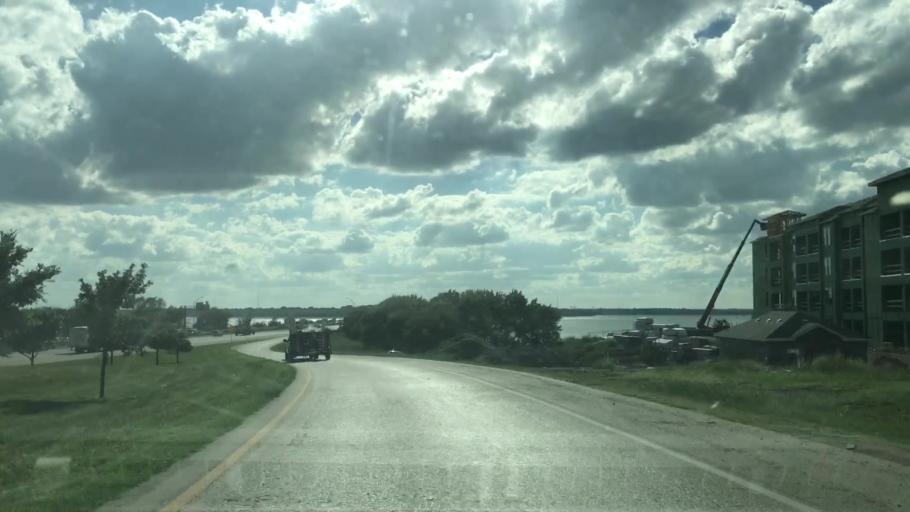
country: US
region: Texas
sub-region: Dallas County
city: Rowlett
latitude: 32.8757
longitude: -96.5211
